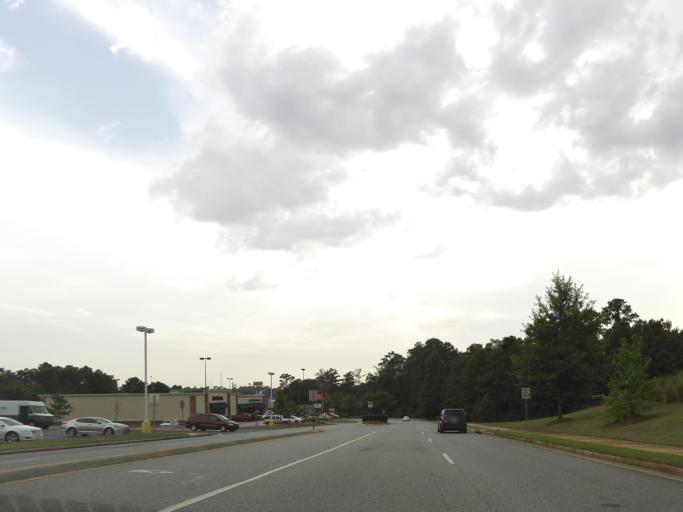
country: US
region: Georgia
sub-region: Bibb County
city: Macon
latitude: 32.8163
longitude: -83.7159
